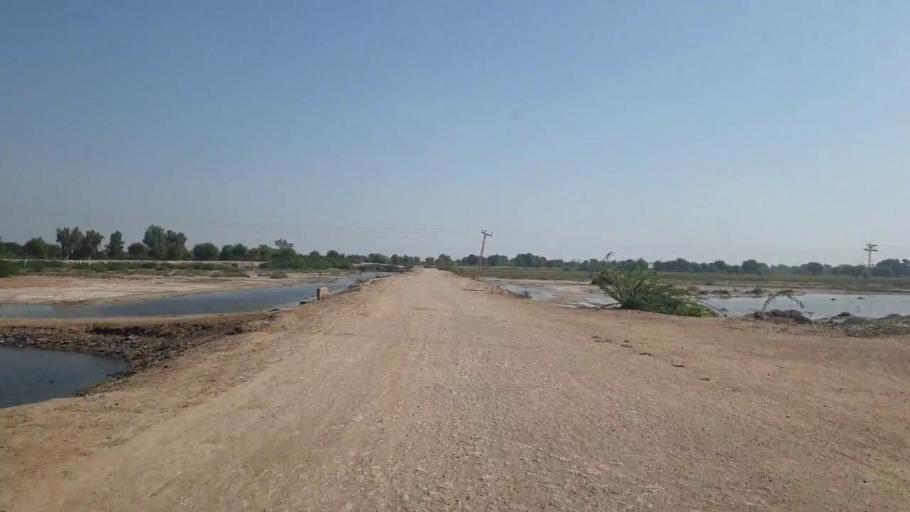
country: PK
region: Sindh
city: Talhar
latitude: 24.7916
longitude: 68.8003
